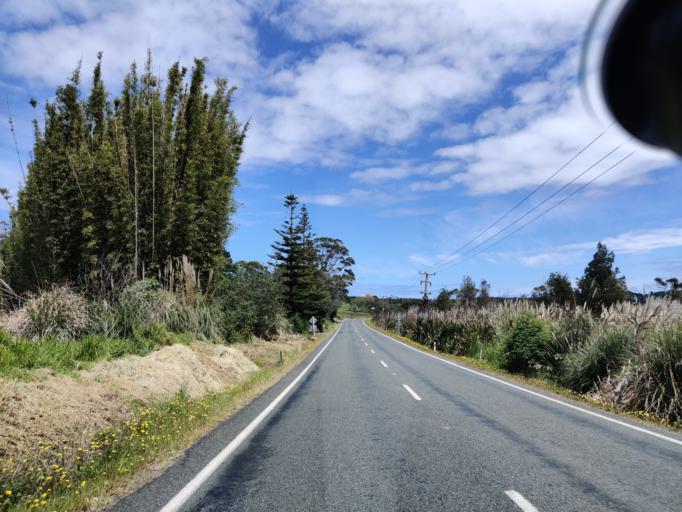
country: NZ
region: Northland
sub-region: Far North District
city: Kaitaia
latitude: -35.0108
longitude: 173.2056
